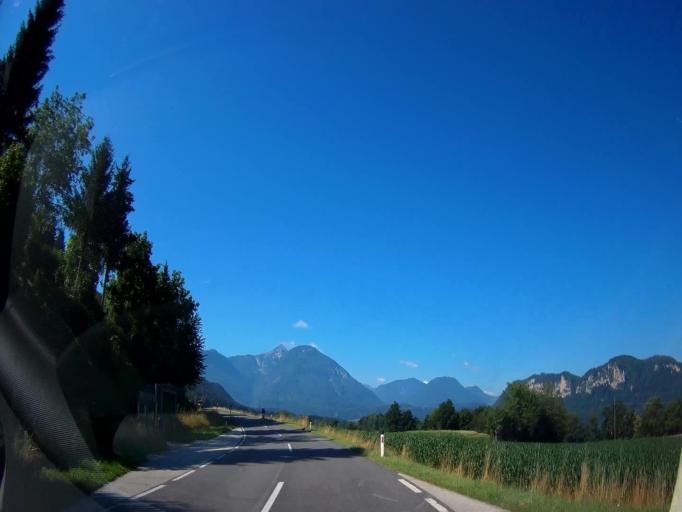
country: AT
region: Carinthia
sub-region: Politischer Bezirk Volkermarkt
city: Gallizien
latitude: 46.5999
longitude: 14.5296
